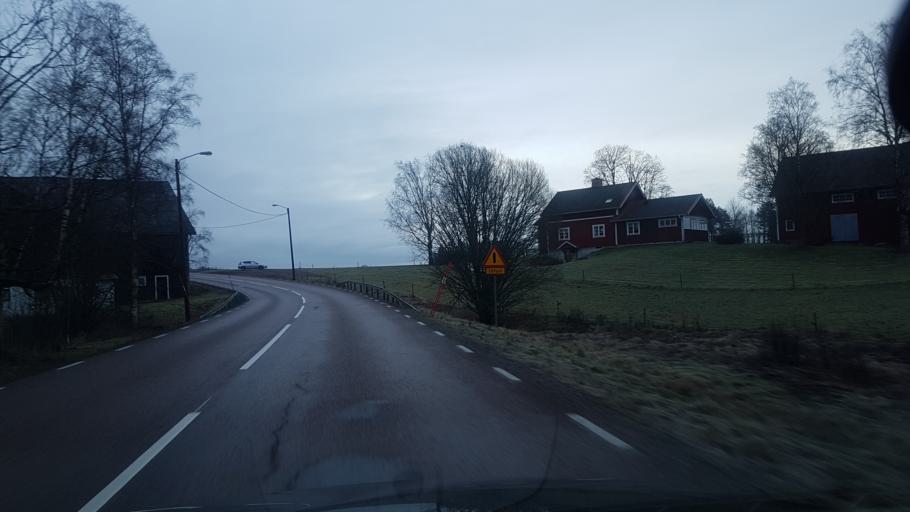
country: SE
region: Dalarna
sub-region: Saters Kommun
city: Saeter
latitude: 60.4169
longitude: 15.7368
